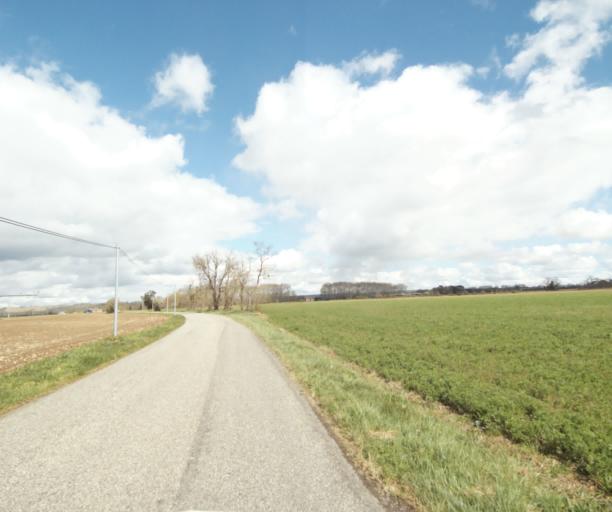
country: FR
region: Midi-Pyrenees
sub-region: Departement de l'Ariege
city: Saverdun
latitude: 43.2530
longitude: 1.5979
